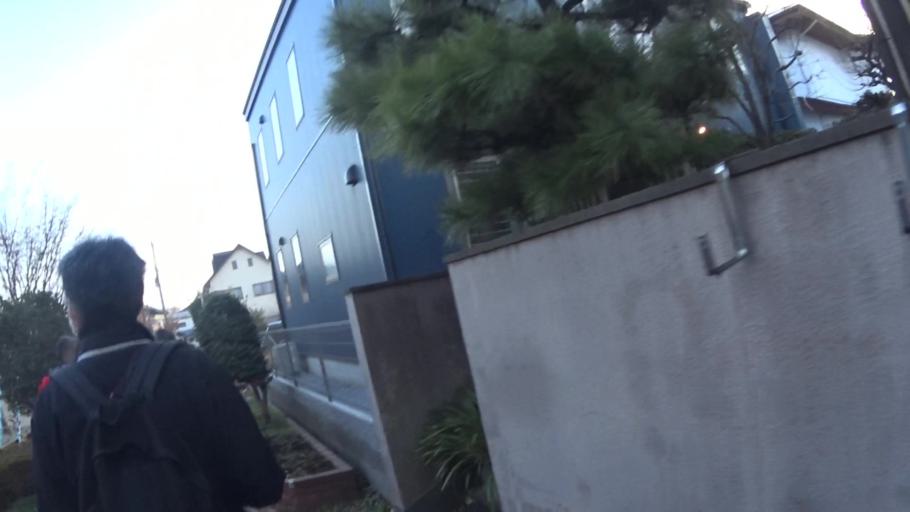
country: JP
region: Saitama
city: Saitama
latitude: 35.9244
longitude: 139.6263
